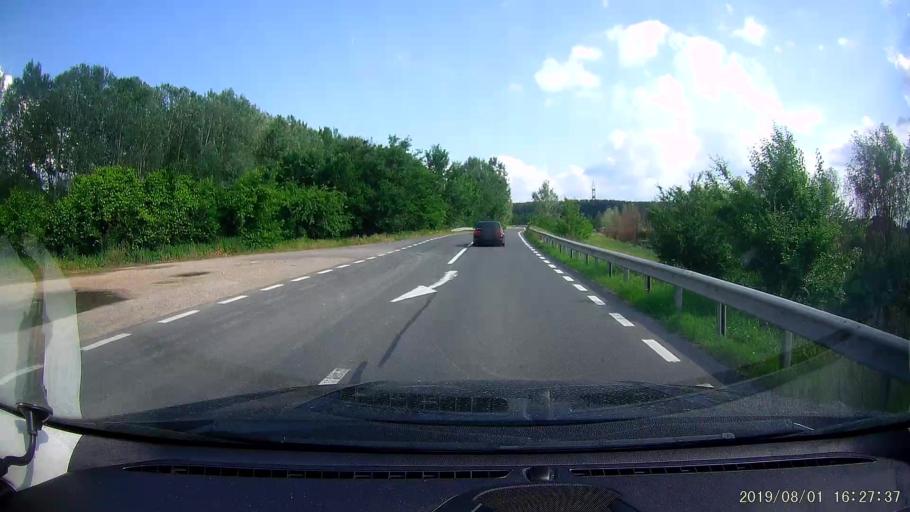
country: RO
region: Calarasi
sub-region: Municipiul Calarasi
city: Calarasi
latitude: 44.1614
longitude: 27.3158
